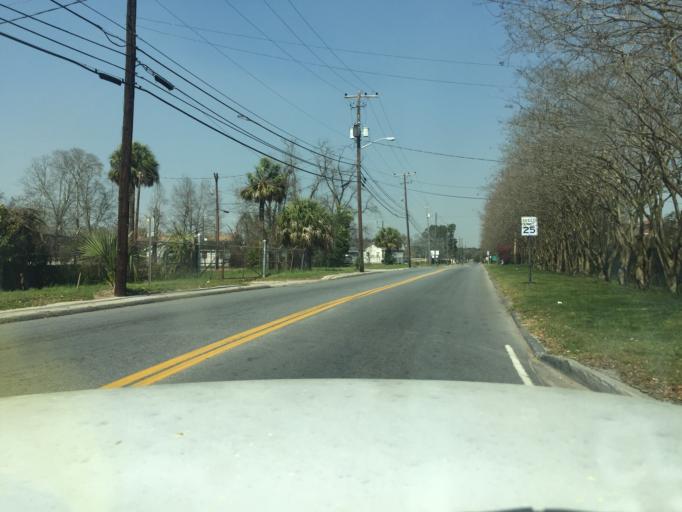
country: US
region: Georgia
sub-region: Chatham County
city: Savannah
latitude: 32.0720
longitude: -81.1140
